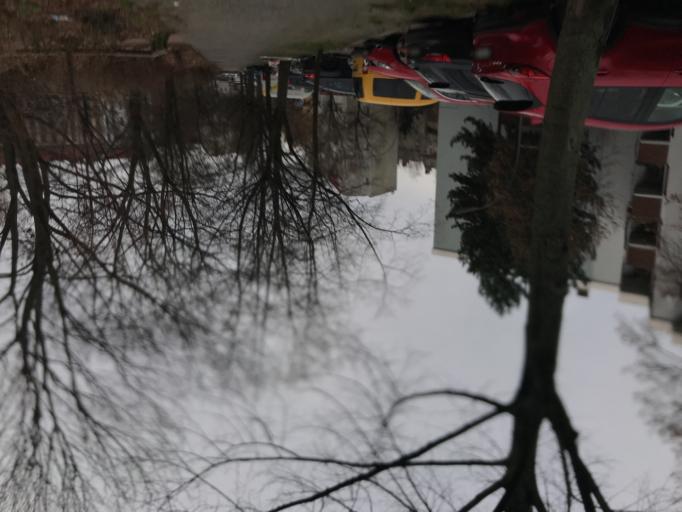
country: DE
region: Berlin
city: Berlin Treptow
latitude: 52.4744
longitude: 13.4377
